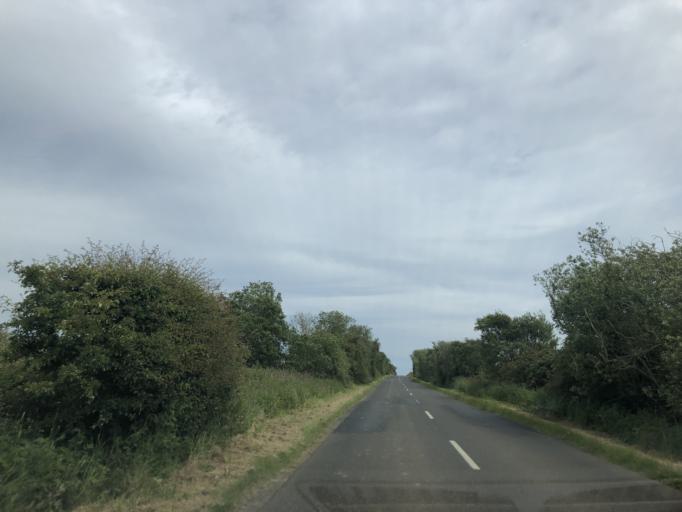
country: GB
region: Scotland
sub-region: Fife
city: Anstruther
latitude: 56.2607
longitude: -2.6790
